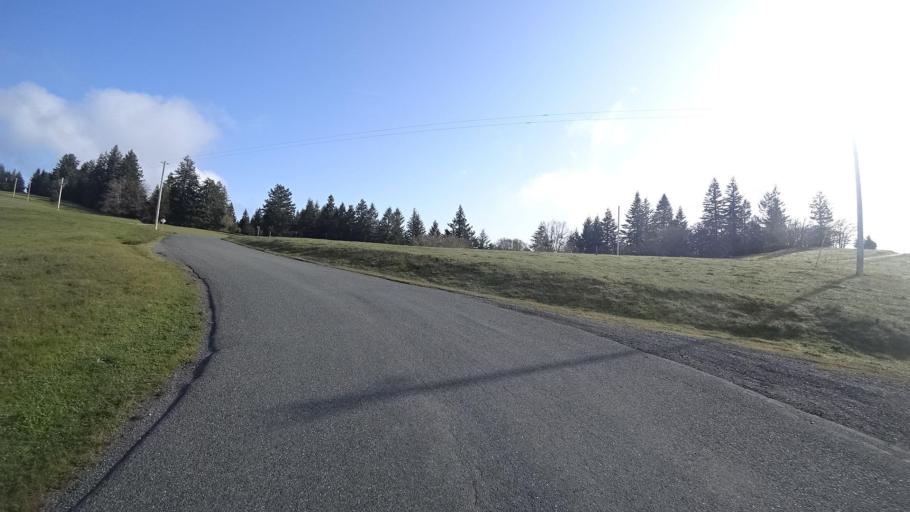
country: US
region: California
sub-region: Humboldt County
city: Blue Lake
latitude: 40.7202
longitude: -123.9424
